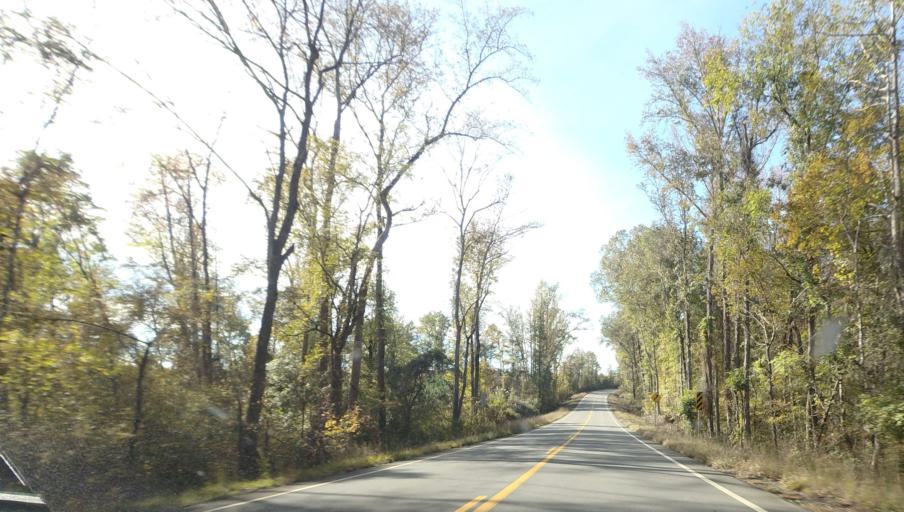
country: US
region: Georgia
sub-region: Taylor County
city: Butler
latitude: 32.7156
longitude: -84.2428
